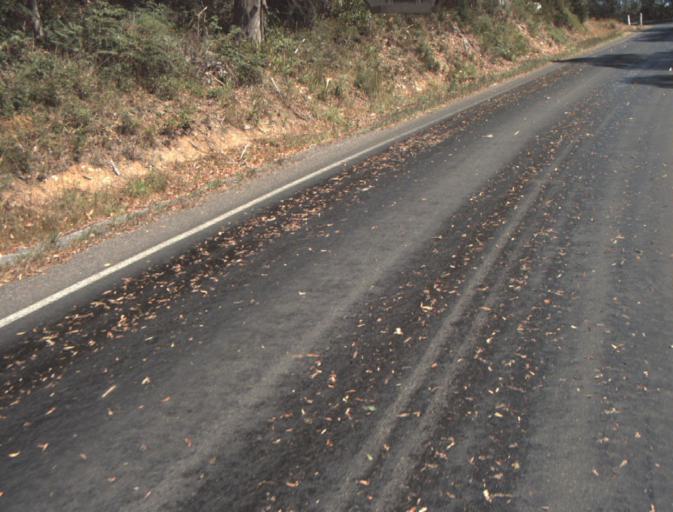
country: AU
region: Tasmania
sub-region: Launceston
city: Newstead
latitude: -41.3244
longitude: 147.3597
